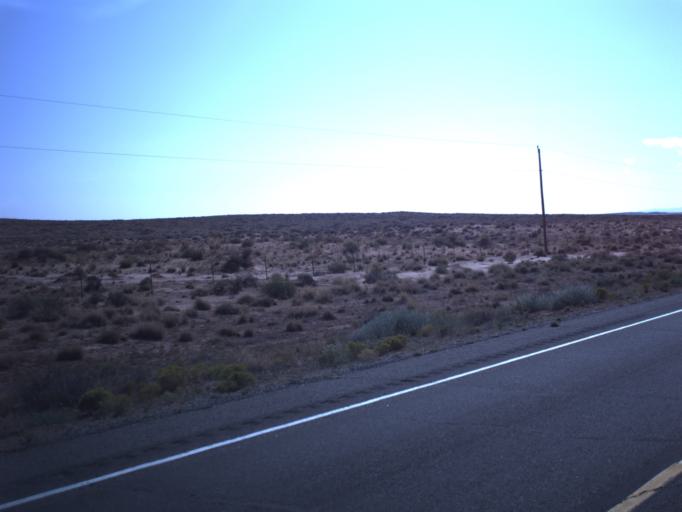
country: US
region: Utah
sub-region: San Juan County
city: Blanding
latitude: 37.1346
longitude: -109.5538
